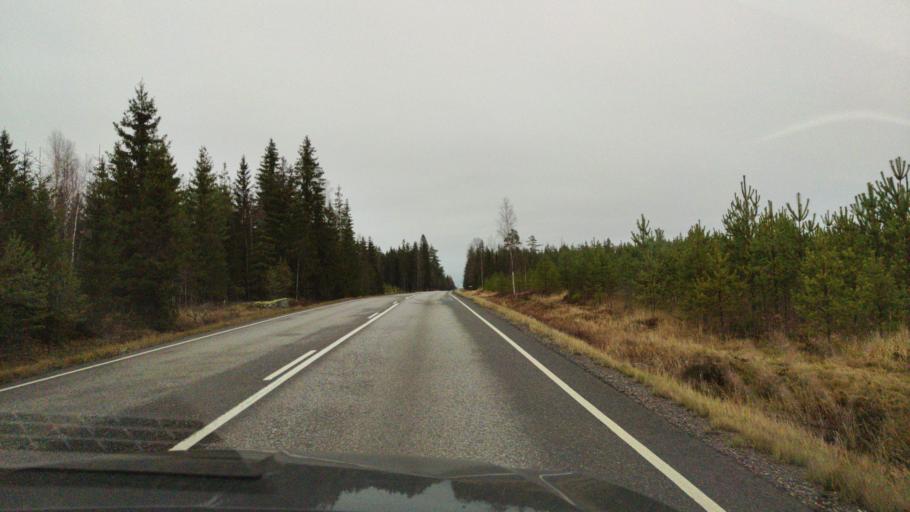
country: FI
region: Varsinais-Suomi
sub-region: Loimaa
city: Ylaene
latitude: 60.7618
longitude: 22.4322
